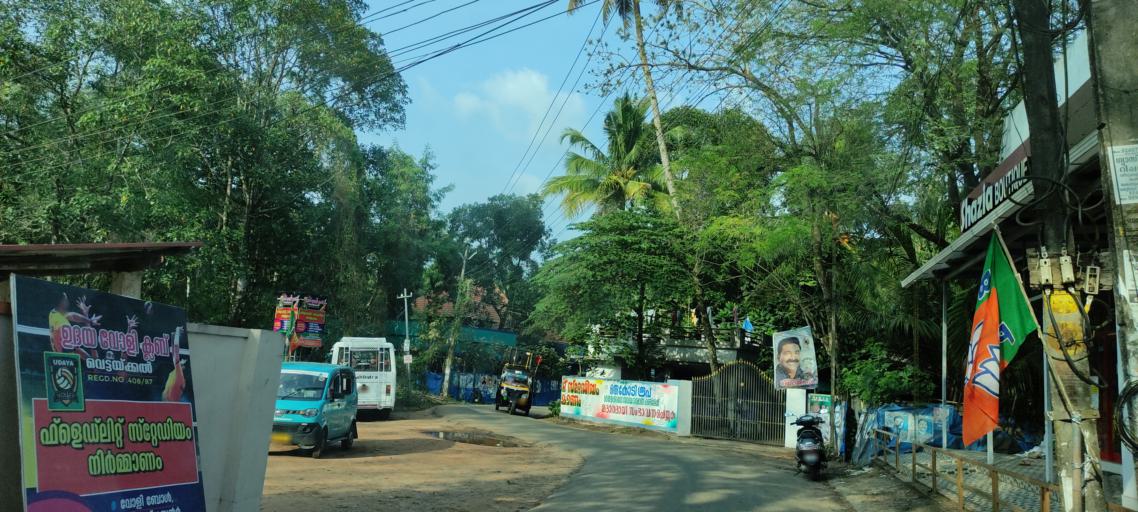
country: IN
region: Kerala
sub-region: Alappuzha
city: Vayalar
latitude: 9.7278
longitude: 76.3005
